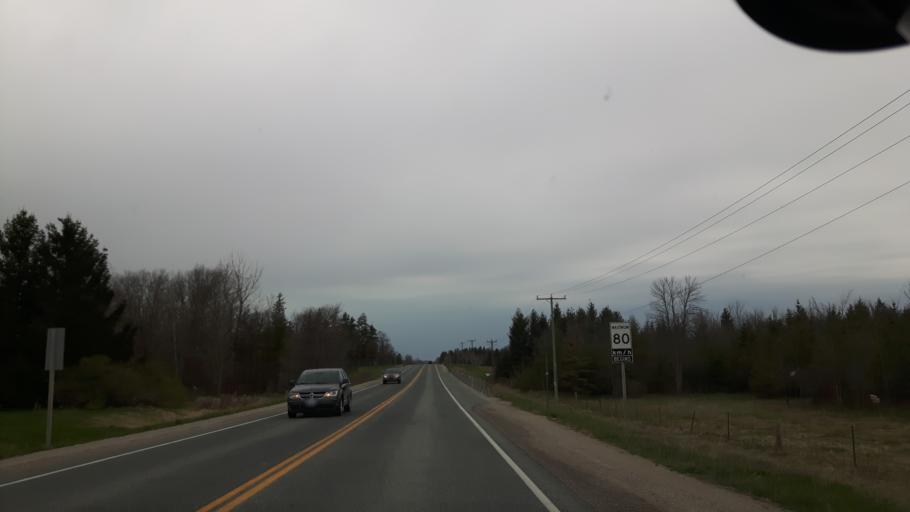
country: CA
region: Ontario
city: Bluewater
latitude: 43.6236
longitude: -81.5547
